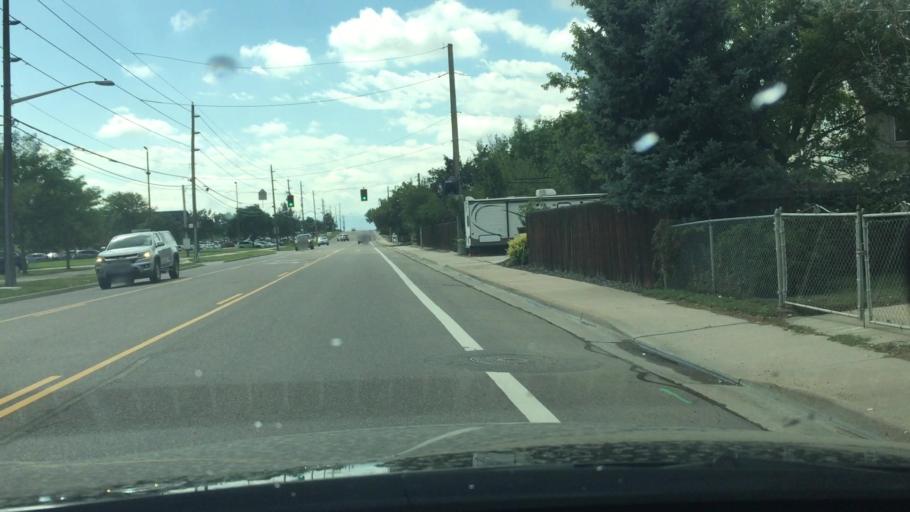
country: US
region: Colorado
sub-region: Jefferson County
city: Lakewood
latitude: 39.6799
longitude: -105.1097
